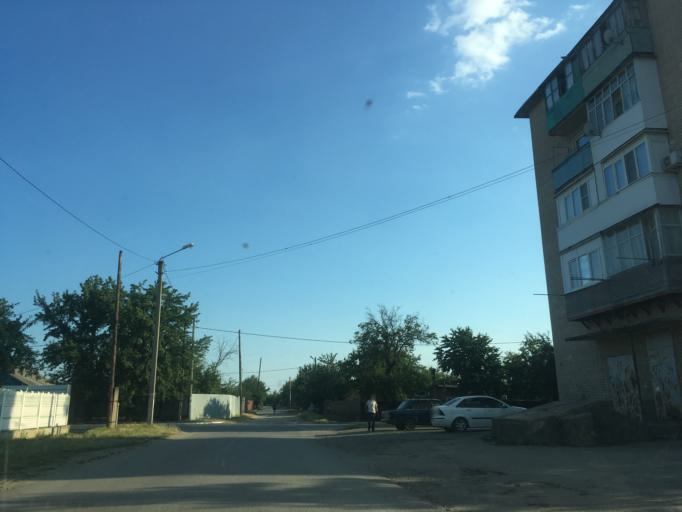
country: RU
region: Rostov
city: Masalovka
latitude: 48.4012
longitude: 40.2771
